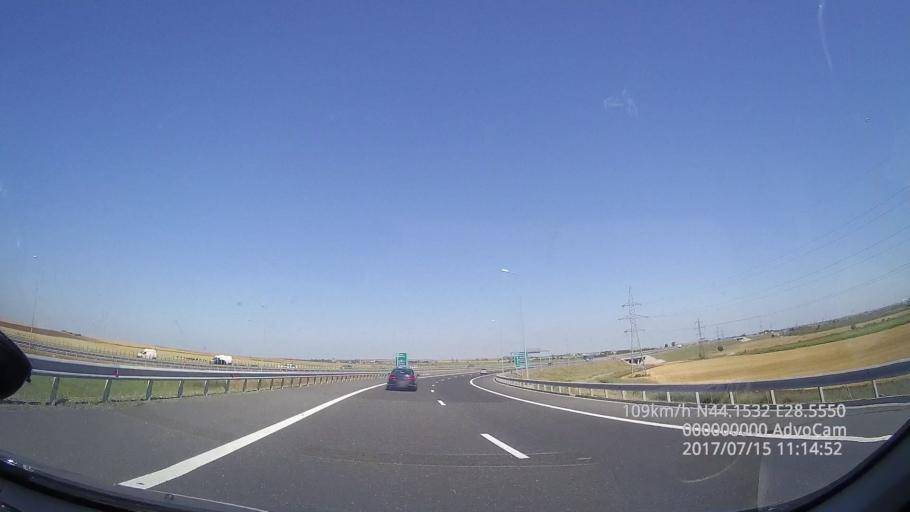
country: RO
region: Constanta
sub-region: Comuna Cumpana
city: Cumpana
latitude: 44.1535
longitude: 28.5540
